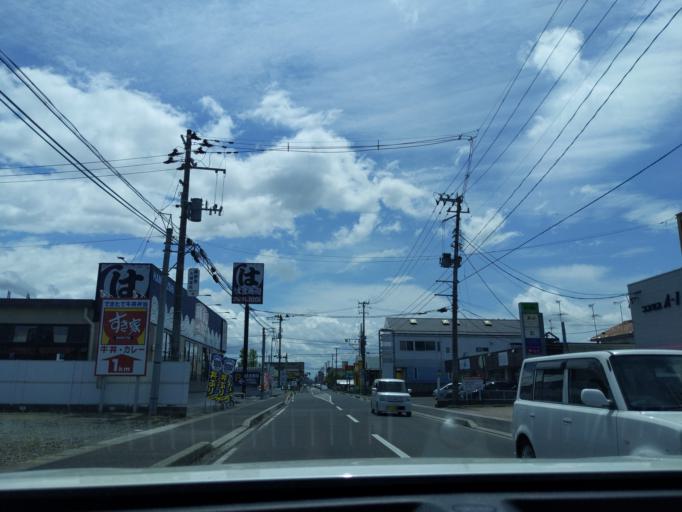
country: JP
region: Fukushima
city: Koriyama
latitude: 37.4003
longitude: 140.3343
